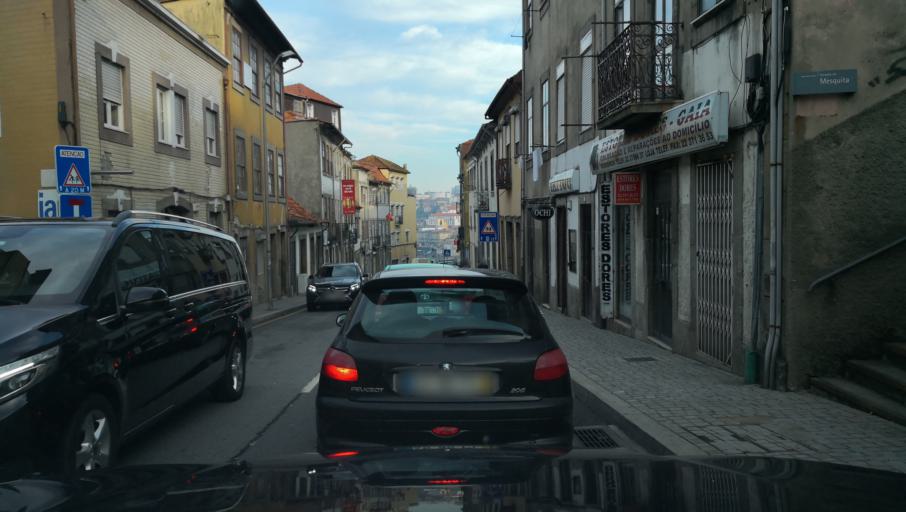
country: PT
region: Porto
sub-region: Vila Nova de Gaia
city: Vila Nova de Gaia
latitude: 41.1347
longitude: -8.6108
